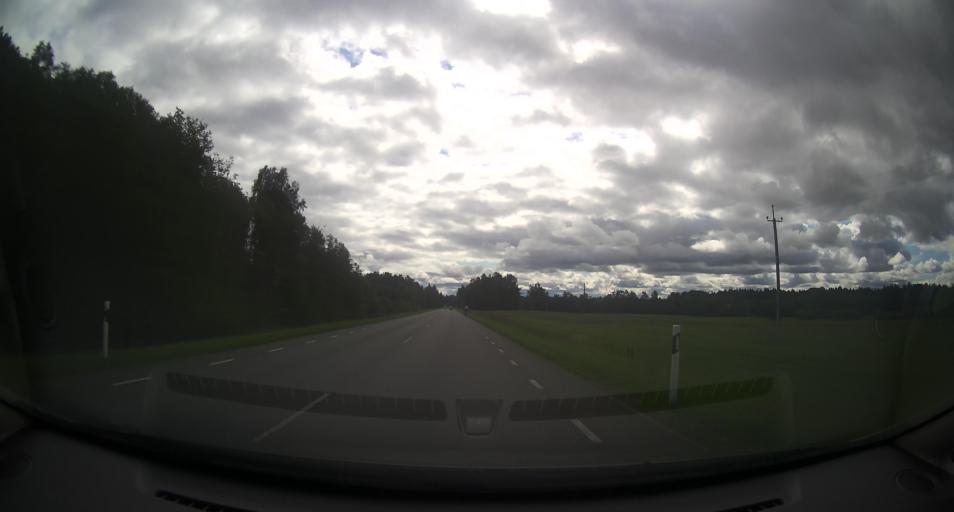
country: EE
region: Harju
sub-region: Raasiku vald
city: Raasiku
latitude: 59.2012
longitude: 25.1852
